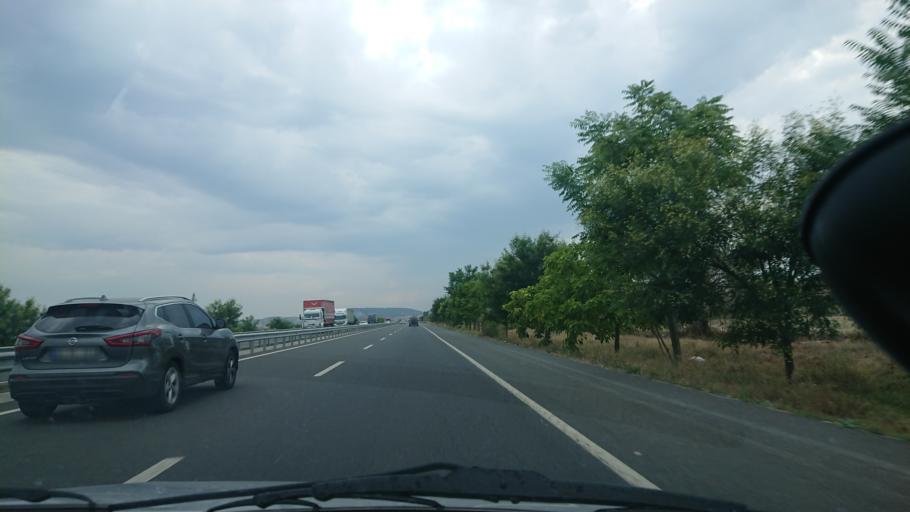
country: TR
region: Manisa
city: Selendi
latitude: 38.6200
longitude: 28.9090
